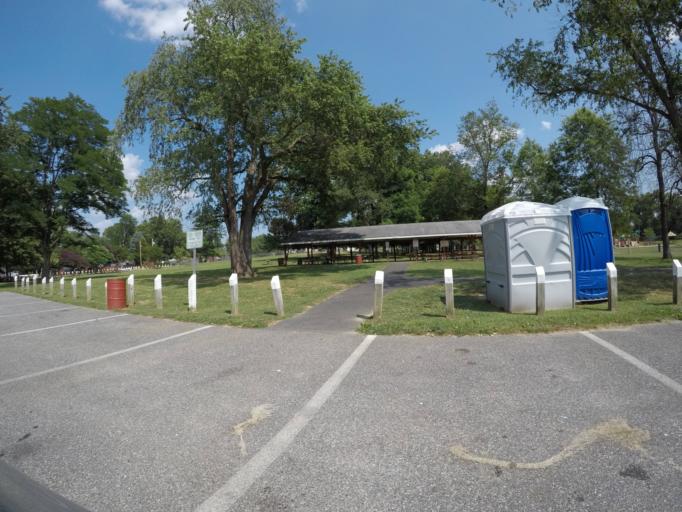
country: US
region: Maryland
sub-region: Harford County
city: Riverside
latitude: 39.4417
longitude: -76.2581
